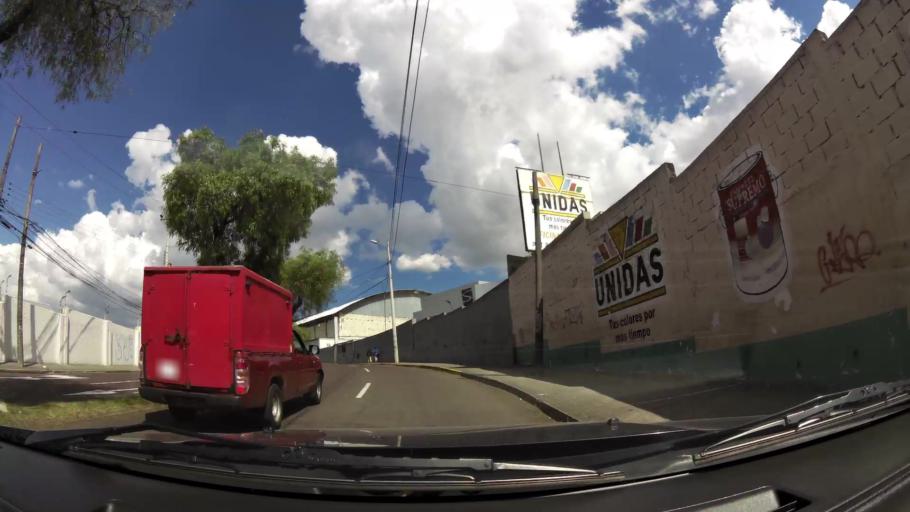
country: EC
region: Pichincha
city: Quito
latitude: -0.0993
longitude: -78.4738
